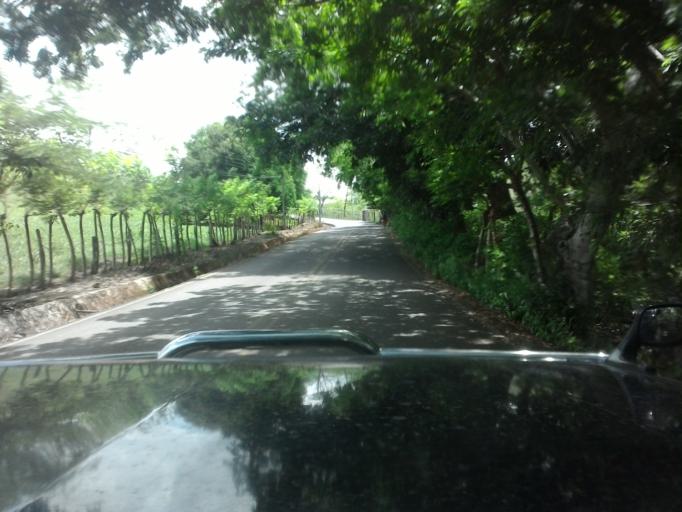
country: CR
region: Puntarenas
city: Miramar
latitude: 10.1400
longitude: -84.8452
